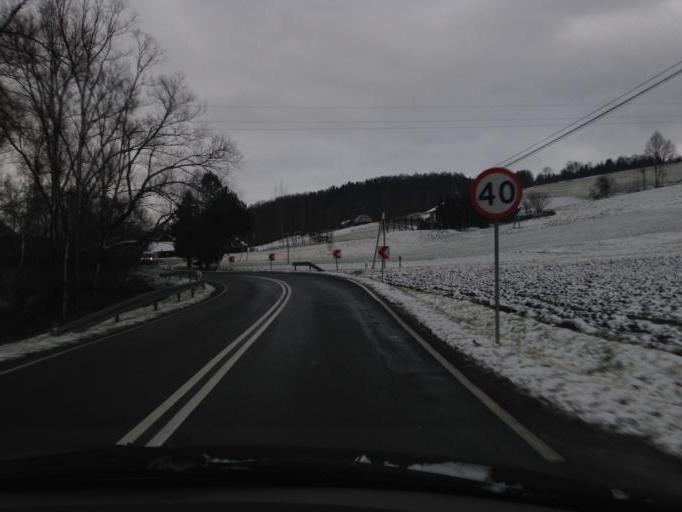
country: PL
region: Lesser Poland Voivodeship
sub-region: Powiat tarnowski
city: Rzepiennik Strzyzewski
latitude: 49.8108
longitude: 21.0176
